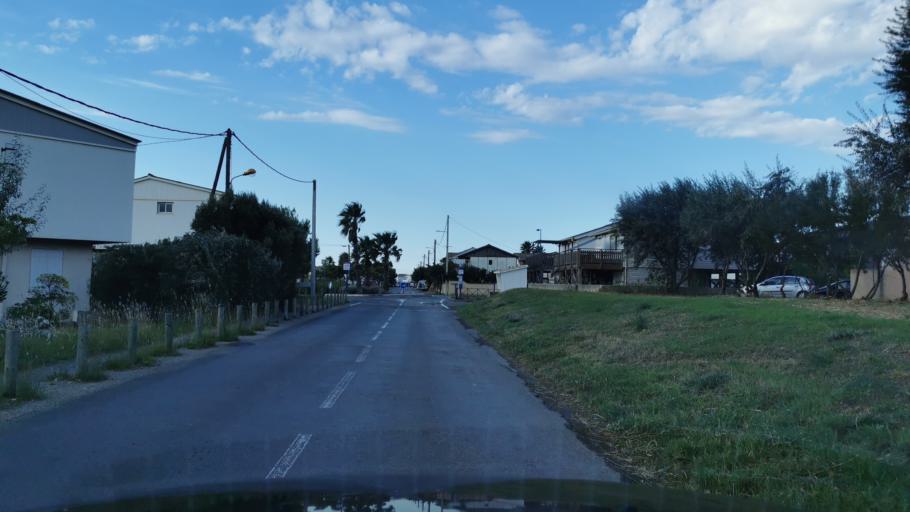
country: FR
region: Languedoc-Roussillon
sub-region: Departement de l'Aude
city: Gruissan
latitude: 43.1014
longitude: 3.1109
